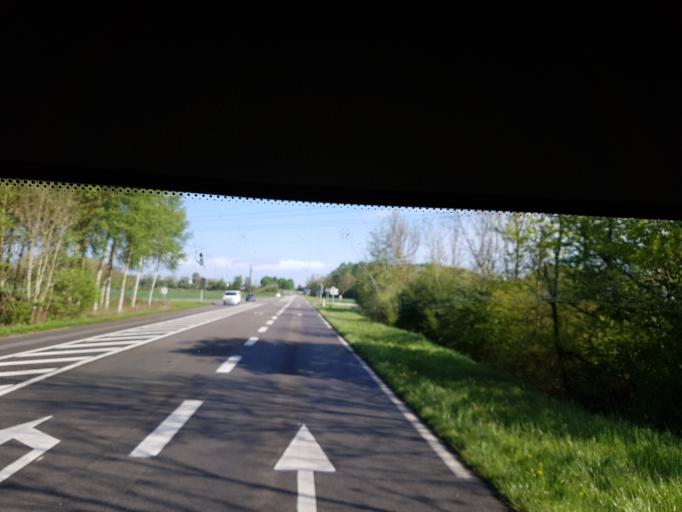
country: FR
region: Picardie
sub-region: Departement de l'Aisne
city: Viry-Noureuil
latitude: 49.6237
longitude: 3.2714
